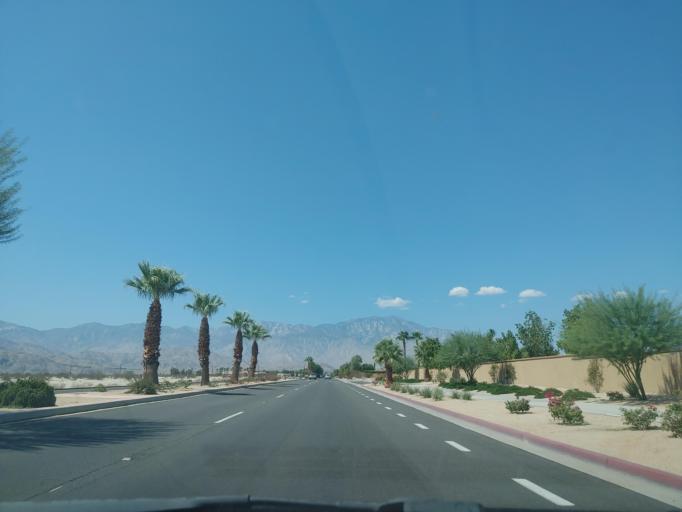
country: US
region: California
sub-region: Riverside County
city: Thousand Palms
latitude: 33.7872
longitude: -116.3985
